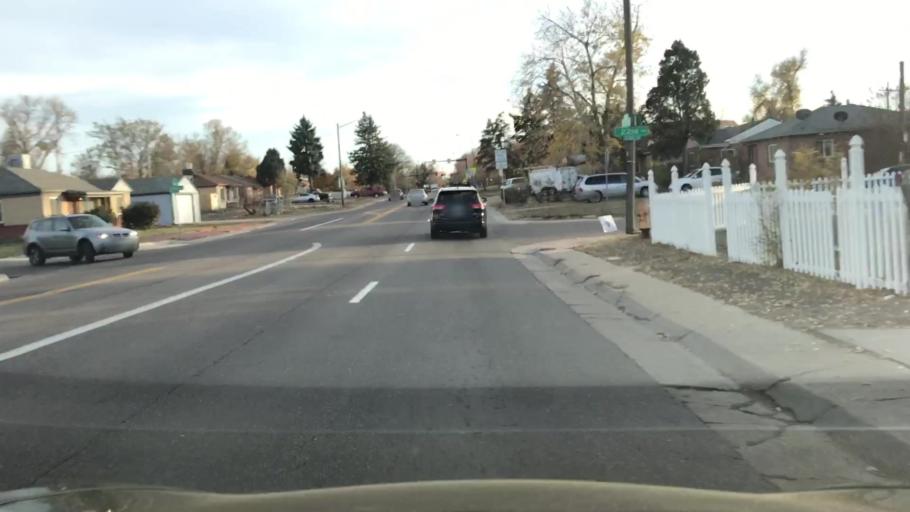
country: US
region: Colorado
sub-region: Arapahoe County
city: Glendale
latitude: 39.7501
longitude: -104.9035
